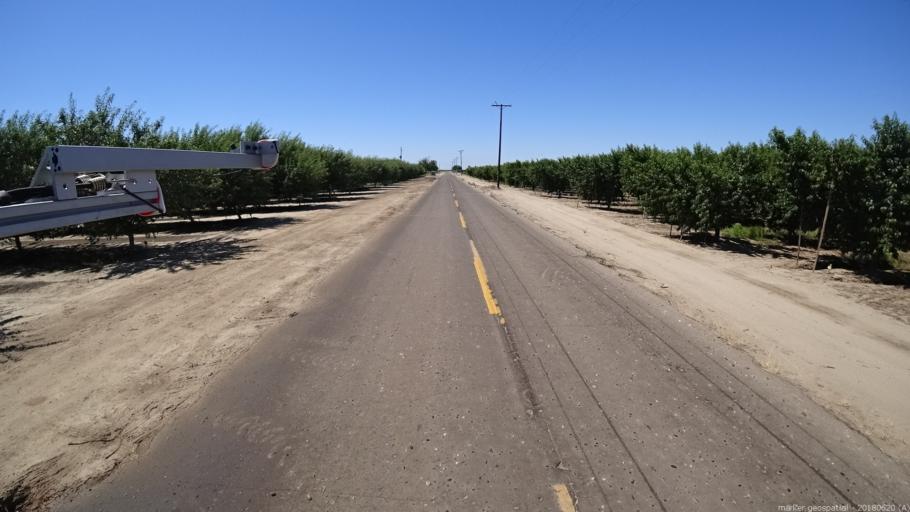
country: US
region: California
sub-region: Fresno County
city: Biola
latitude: 36.8418
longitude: -120.0100
